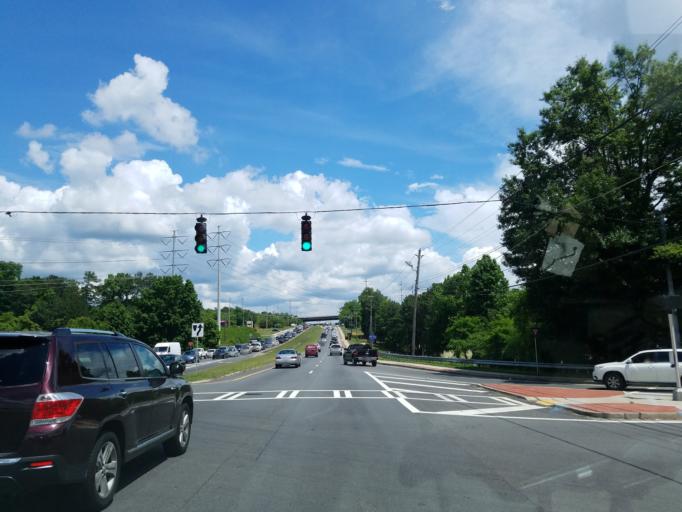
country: US
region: Georgia
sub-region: Cobb County
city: Marietta
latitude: 33.9795
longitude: -84.5547
